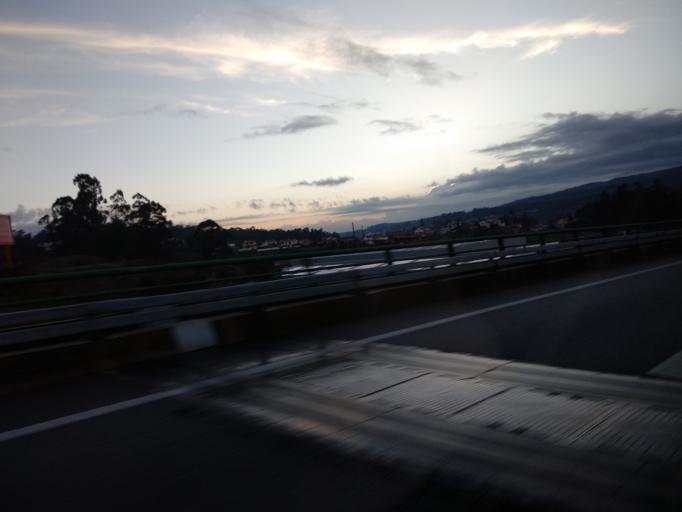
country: PT
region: Braga
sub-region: Braga
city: Oliveira
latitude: 41.4964
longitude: -8.4683
